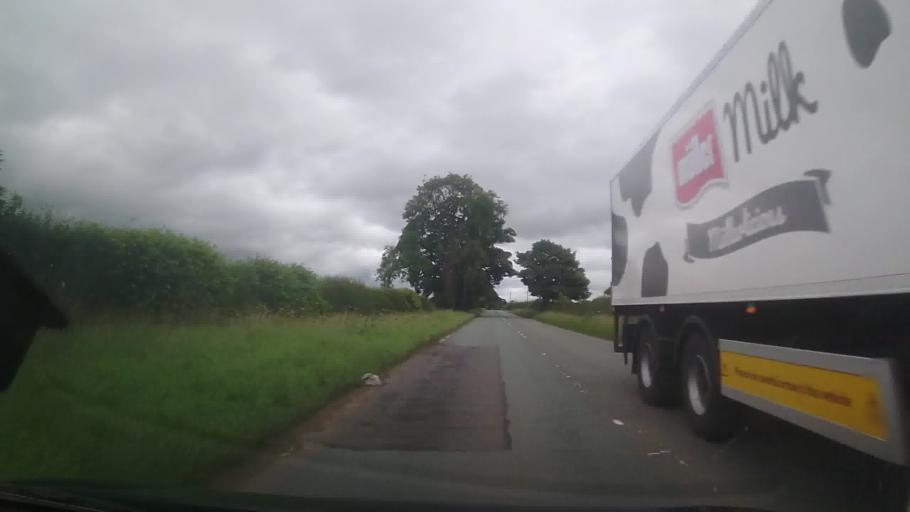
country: GB
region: England
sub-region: Cheshire West and Chester
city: Malpas
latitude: 52.9401
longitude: -2.7846
